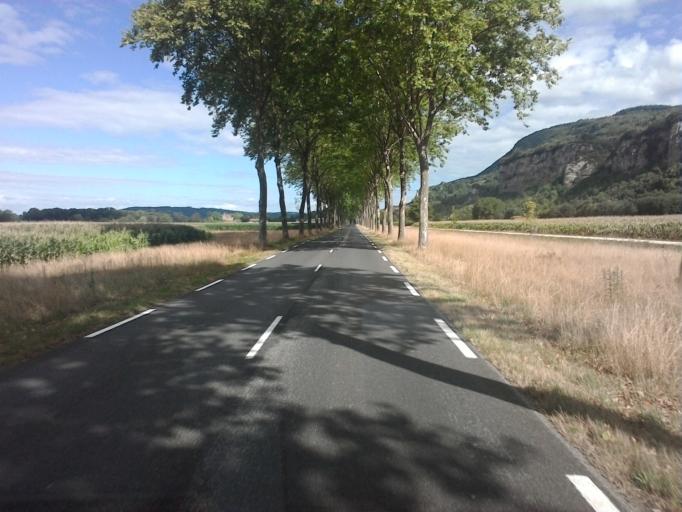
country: FR
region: Rhone-Alpes
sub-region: Departement de l'Ain
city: Saint-Sorlin-en-Bugey
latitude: 45.8733
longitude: 5.3845
